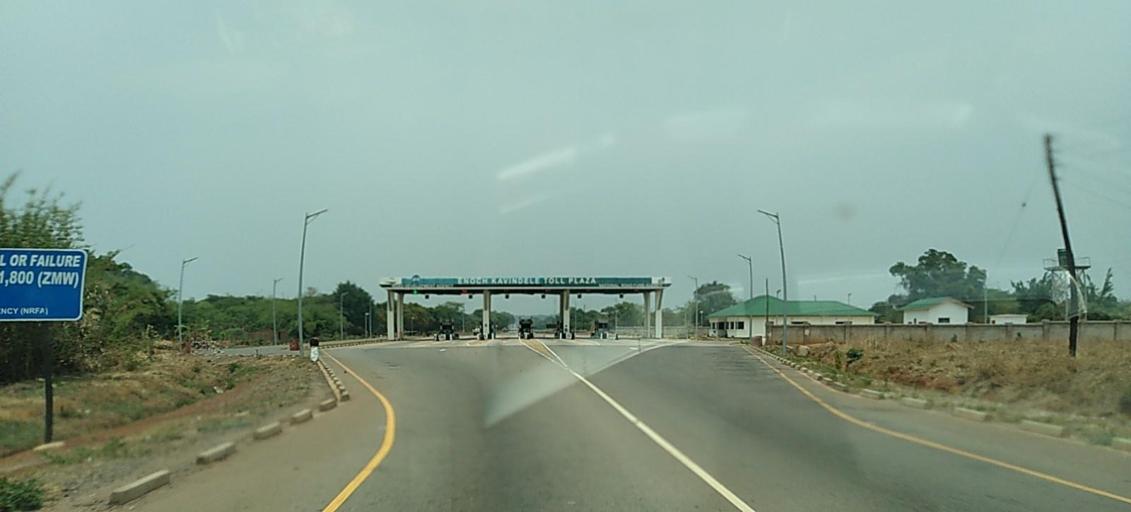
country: ZM
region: Copperbelt
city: Chingola
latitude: -12.5525
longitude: 27.7028
